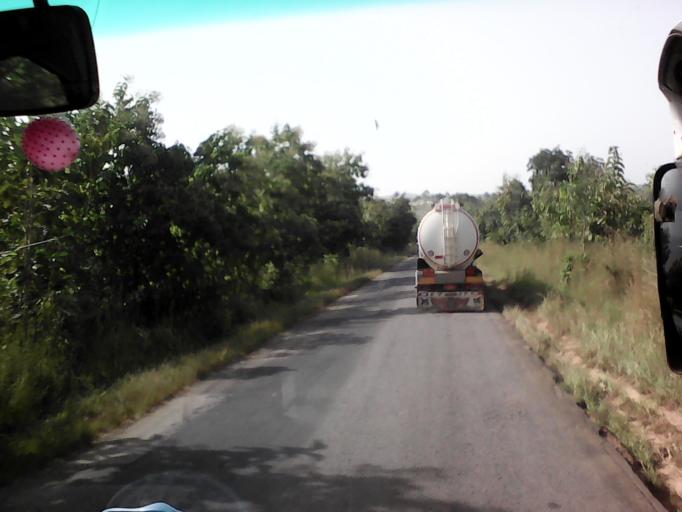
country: TG
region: Centrale
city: Sokode
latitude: 9.0801
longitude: 1.1353
